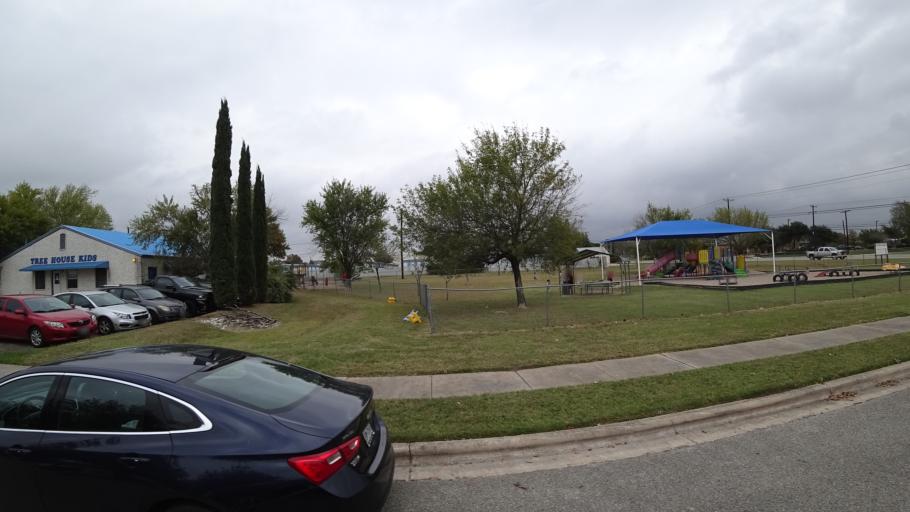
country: US
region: Texas
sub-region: Travis County
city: Pflugerville
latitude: 30.4408
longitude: -97.6120
